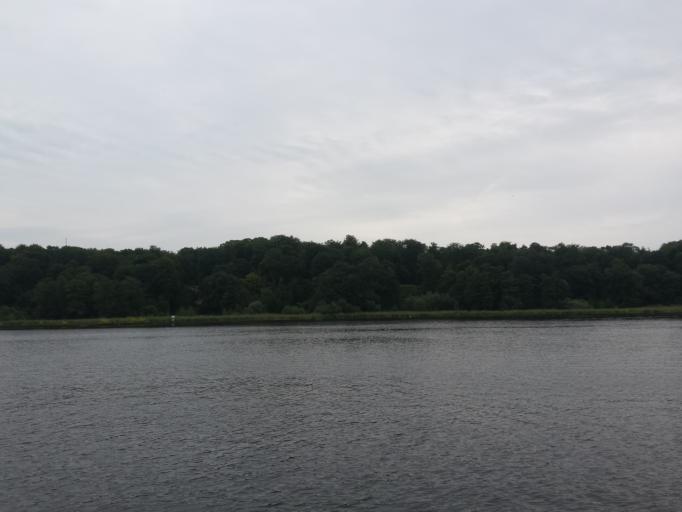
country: DE
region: Brandenburg
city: Potsdam
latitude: 52.4208
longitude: 13.0930
